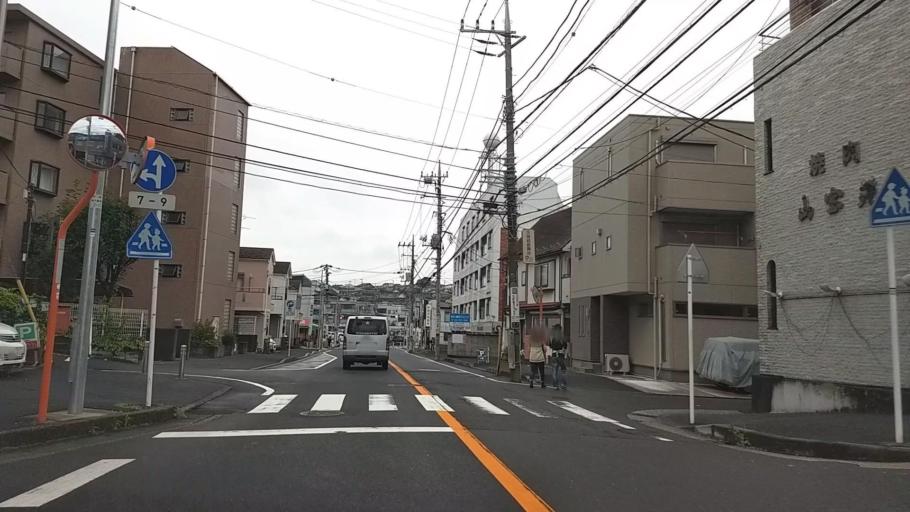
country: JP
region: Kanagawa
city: Yokohama
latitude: 35.4123
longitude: 139.6091
